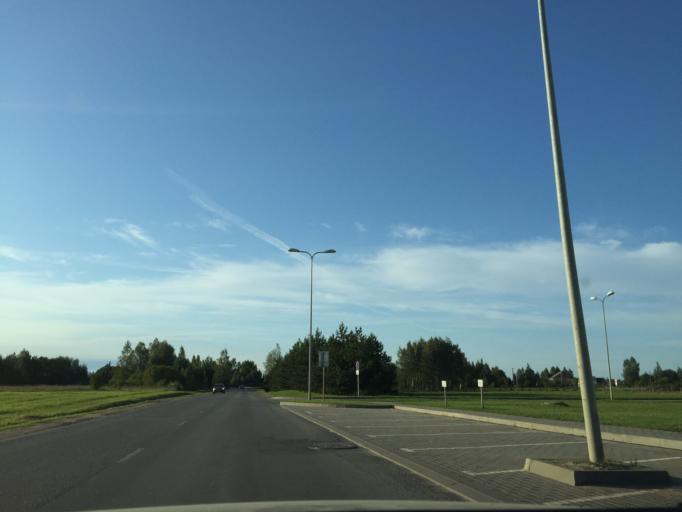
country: LT
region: Panevezys
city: Rokiskis
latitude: 55.9491
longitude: 25.5772
